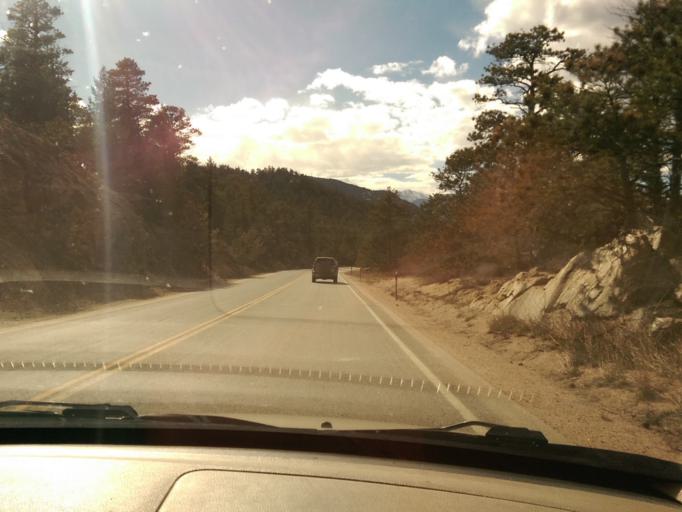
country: US
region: Colorado
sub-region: Larimer County
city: Estes Park
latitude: 40.3669
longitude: -105.4753
